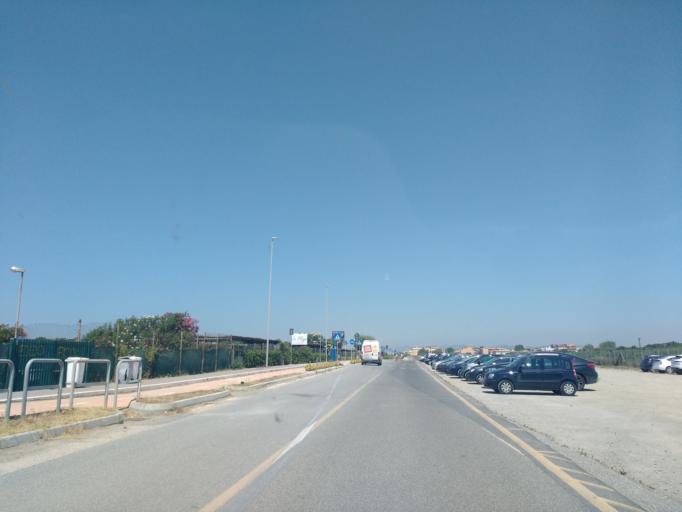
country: IT
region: Latium
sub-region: Citta metropolitana di Roma Capitale
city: Passo Oscuro
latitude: 41.8913
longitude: 12.1659
